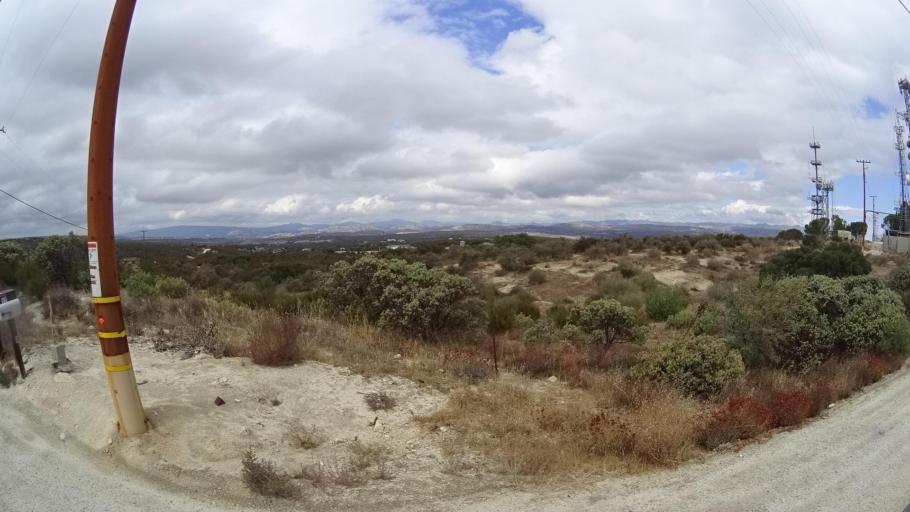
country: US
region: California
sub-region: San Diego County
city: Campo
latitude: 32.6456
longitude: -116.3178
